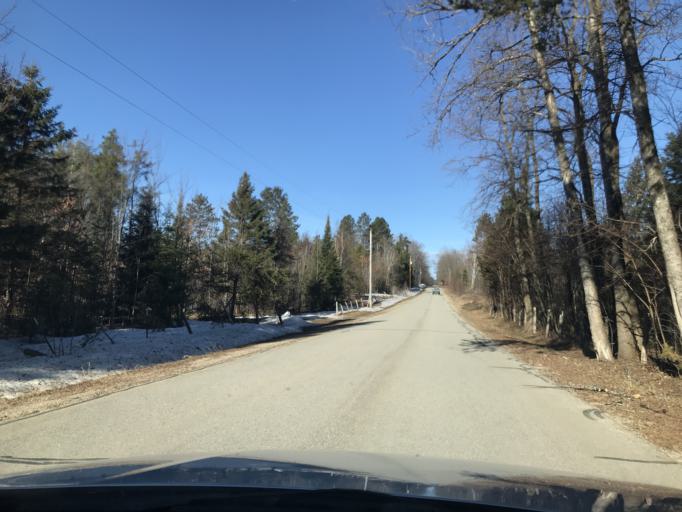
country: US
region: Wisconsin
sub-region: Marinette County
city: Niagara
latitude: 45.3901
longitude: -88.0657
